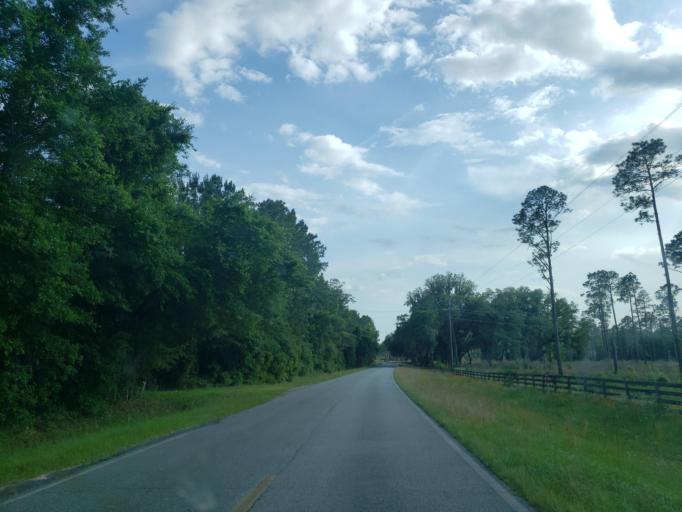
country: US
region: Georgia
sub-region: Echols County
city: Statenville
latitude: 30.6308
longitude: -83.1968
